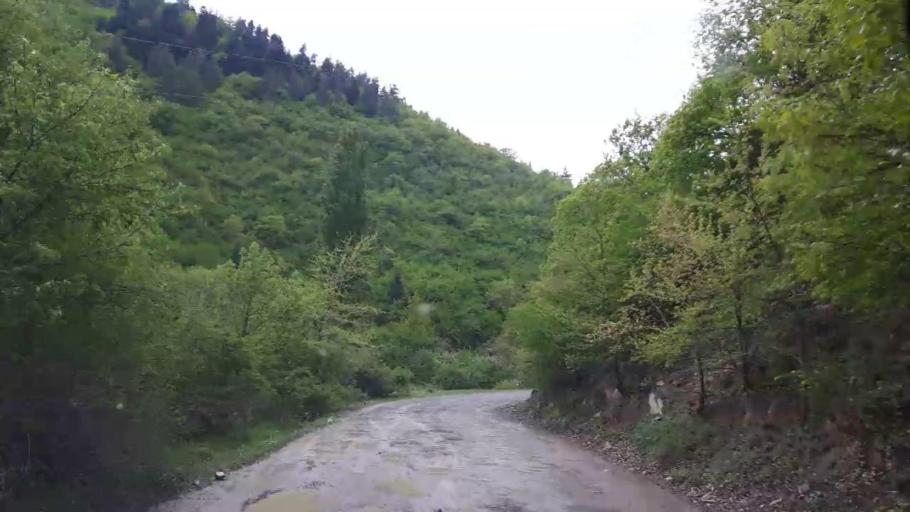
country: GE
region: Shida Kartli
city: Gori
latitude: 41.8800
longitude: 43.9929
